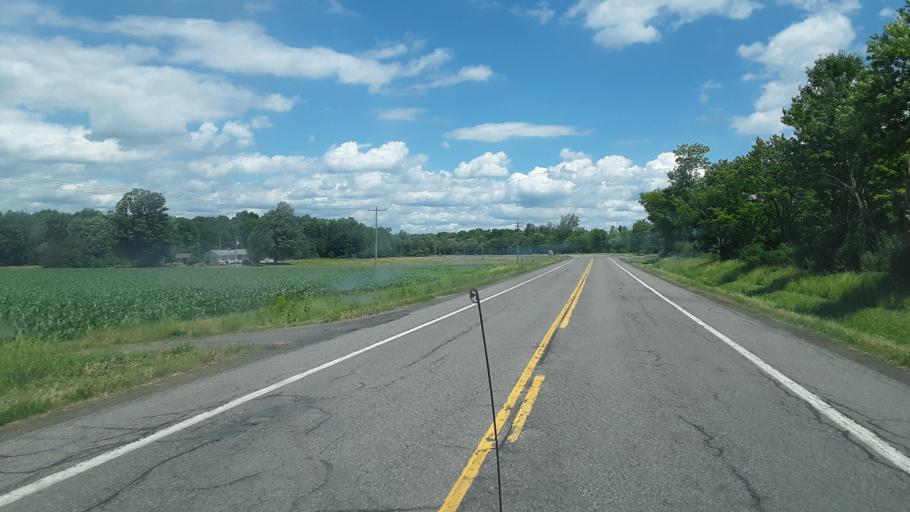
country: US
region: New York
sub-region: Madison County
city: Oneida
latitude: 43.1850
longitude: -75.6335
